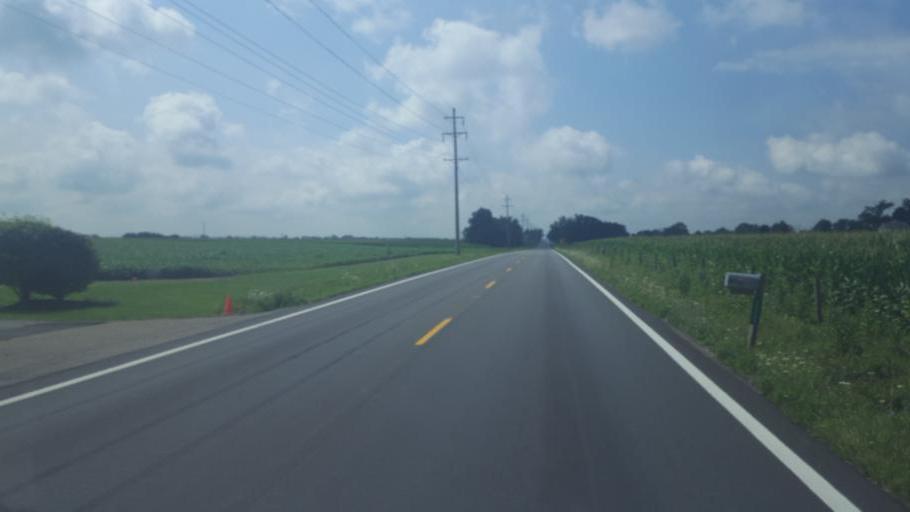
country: US
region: Ohio
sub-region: Fairfield County
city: Millersport
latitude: 39.8766
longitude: -82.5657
